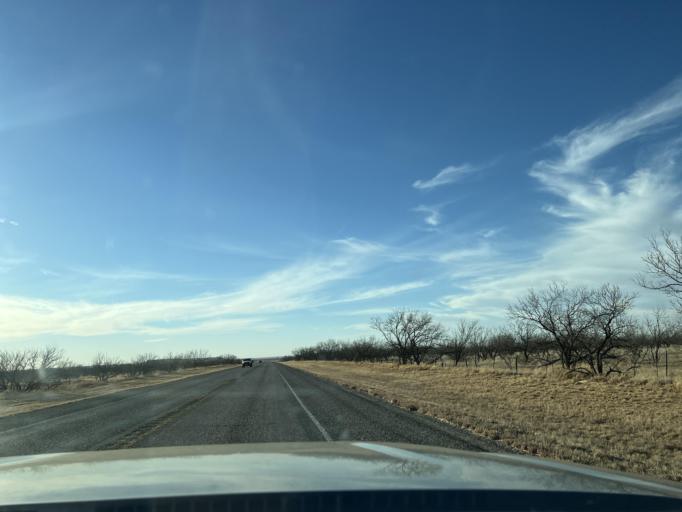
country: US
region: Texas
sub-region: Borden County
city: Gail
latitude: 32.7686
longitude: -101.3132
